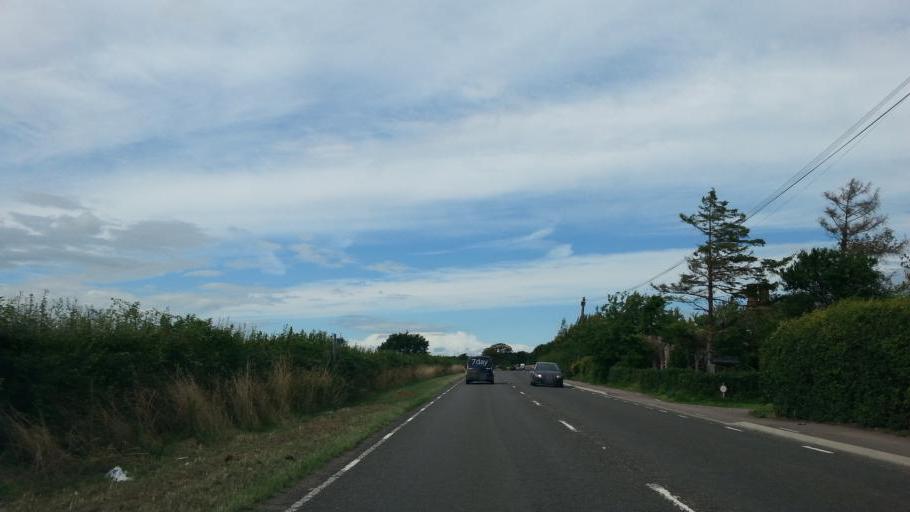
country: GB
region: England
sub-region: Cambridgeshire
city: Sawston
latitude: 52.1445
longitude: 0.1967
